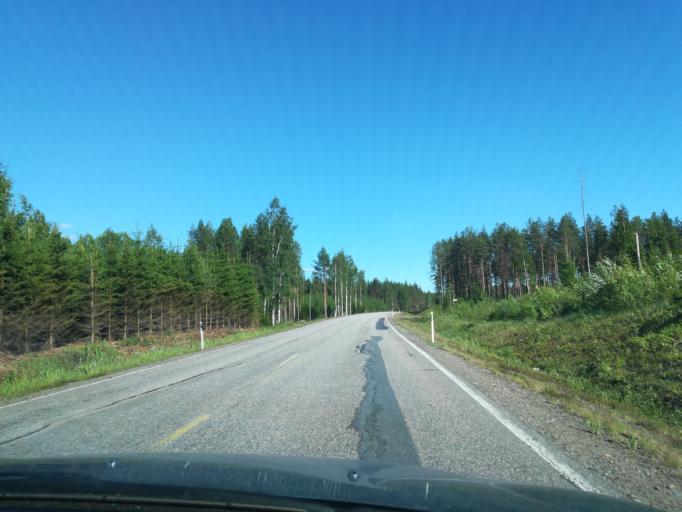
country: FI
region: Southern Savonia
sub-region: Mikkeli
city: Puumala
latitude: 61.4706
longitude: 28.3092
